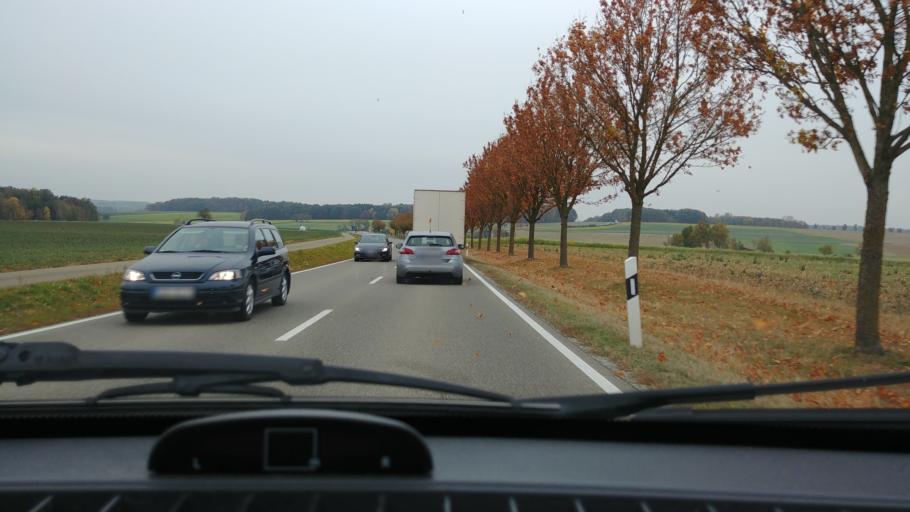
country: DE
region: Baden-Wuerttemberg
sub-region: Regierungsbezirk Stuttgart
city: Schrozberg
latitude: 49.3294
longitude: 9.9317
